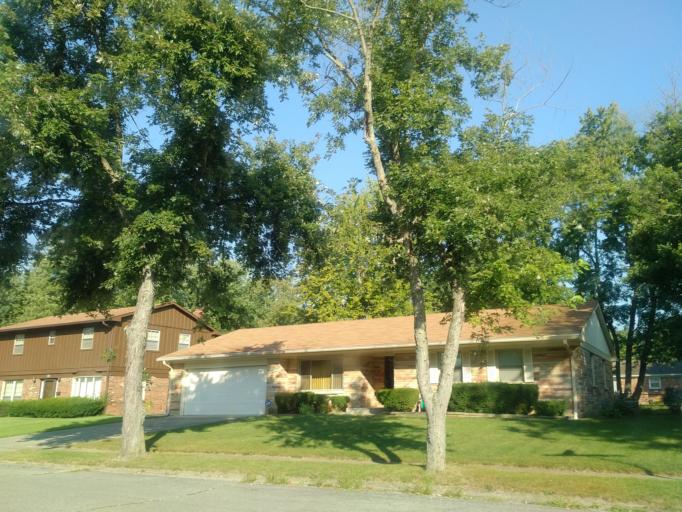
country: US
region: Indiana
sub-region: Marion County
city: Cumberland
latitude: 39.7925
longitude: -85.9822
